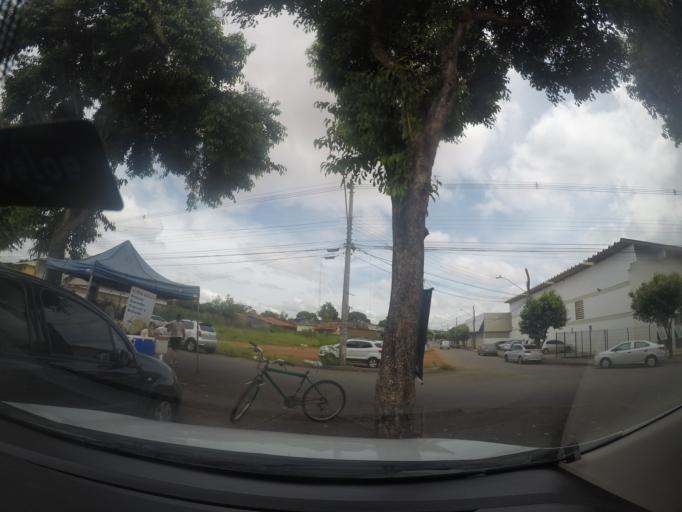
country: BR
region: Goias
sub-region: Goiania
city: Goiania
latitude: -16.7148
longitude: -49.3032
